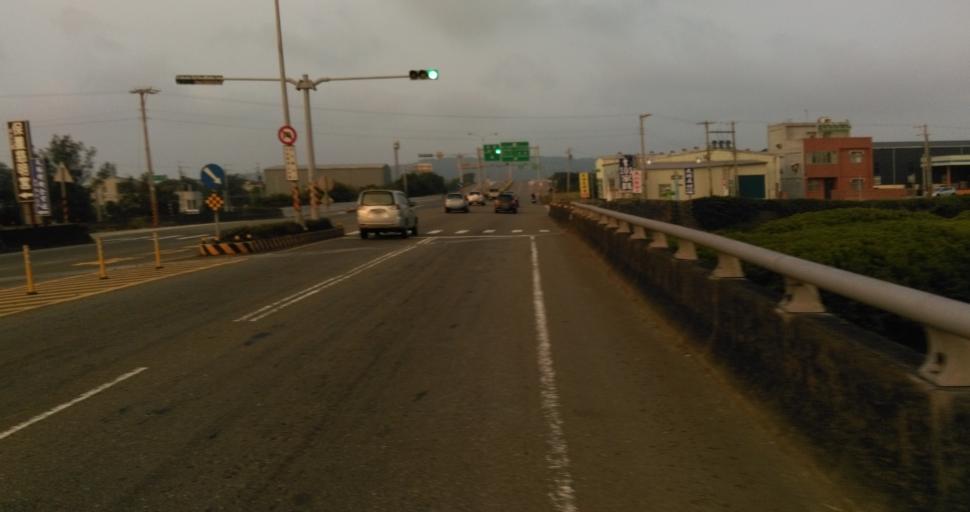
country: TW
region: Taiwan
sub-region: Hsinchu
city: Hsinchu
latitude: 24.8545
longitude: 120.9455
